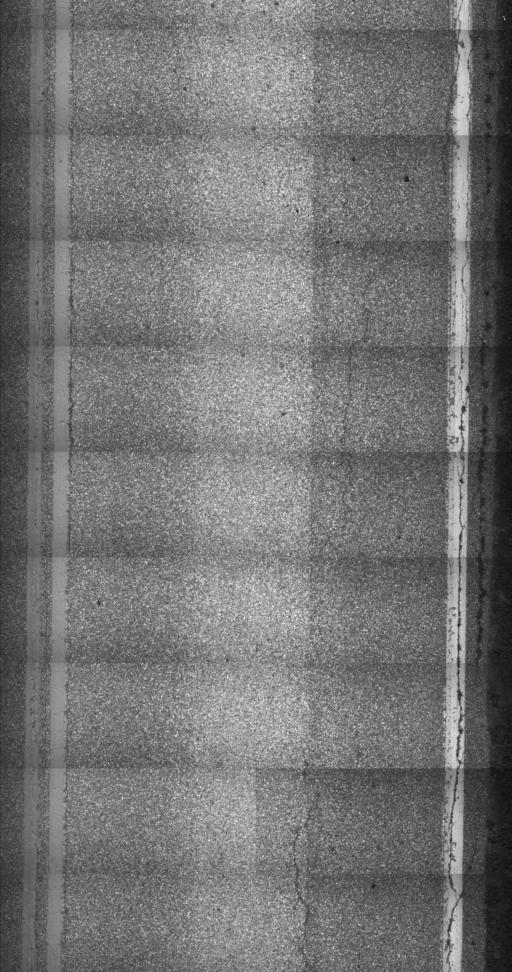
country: US
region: New York
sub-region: Washington County
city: Granville
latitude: 43.4169
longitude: -73.2126
